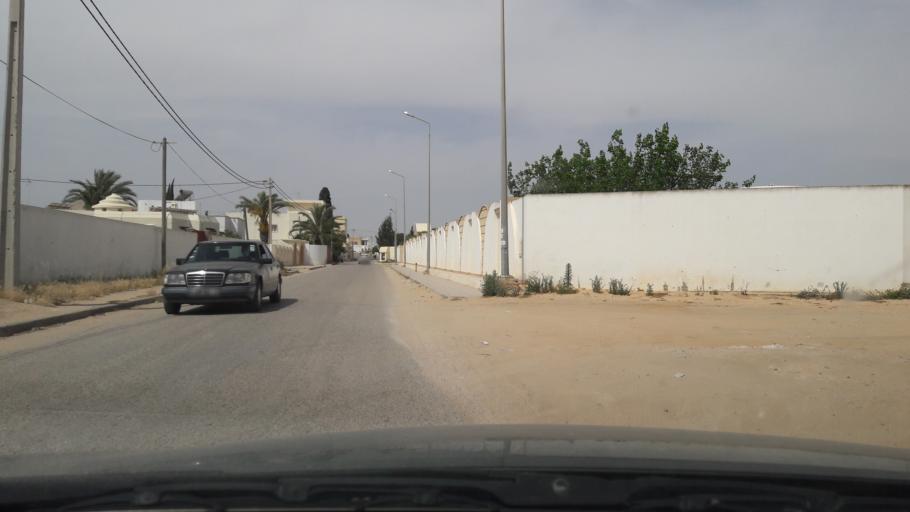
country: TN
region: Safaqis
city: Al Qarmadah
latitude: 34.7859
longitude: 10.7593
